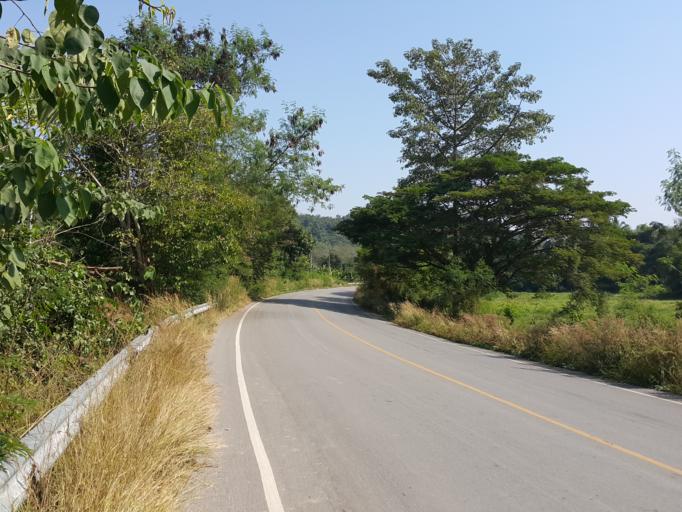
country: TH
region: Sukhothai
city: Thung Saliam
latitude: 17.3429
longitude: 99.4686
